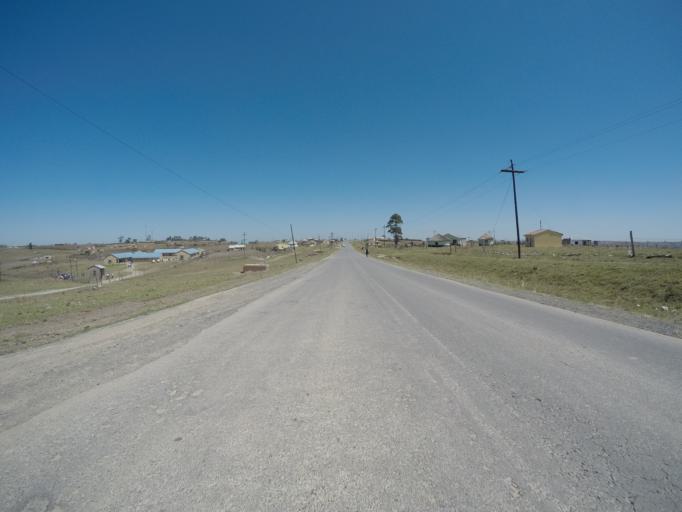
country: ZA
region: Eastern Cape
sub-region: OR Tambo District Municipality
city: Libode
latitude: -31.9185
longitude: 28.9775
